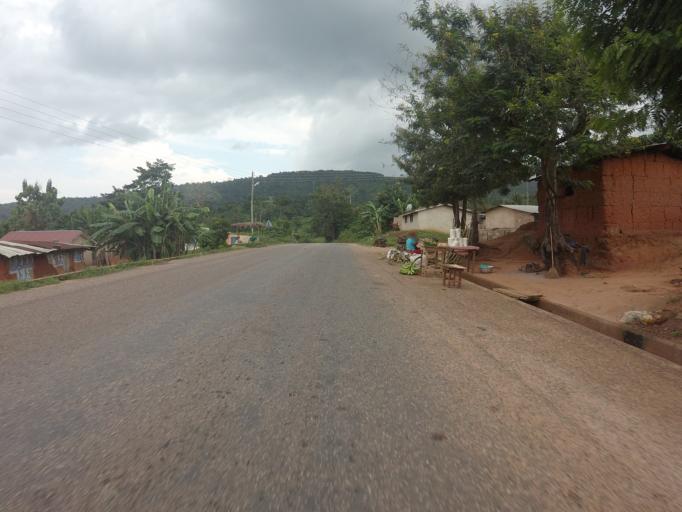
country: GH
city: Akropong
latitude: 5.9582
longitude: -0.1294
